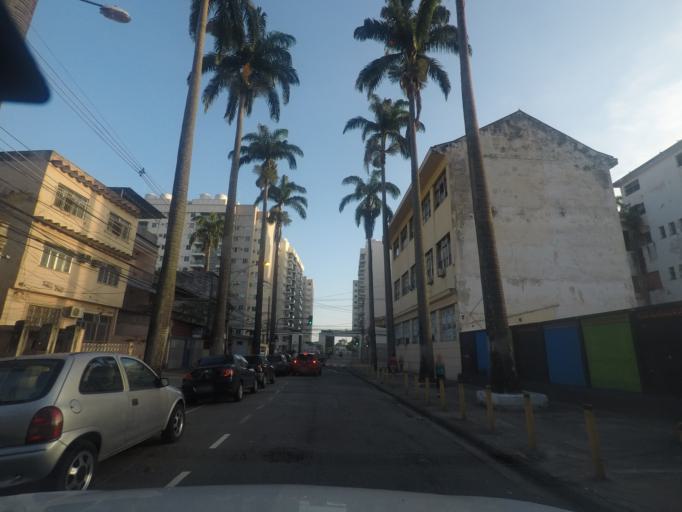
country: BR
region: Rio de Janeiro
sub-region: Duque De Caxias
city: Duque de Caxias
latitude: -22.8385
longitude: -43.2760
